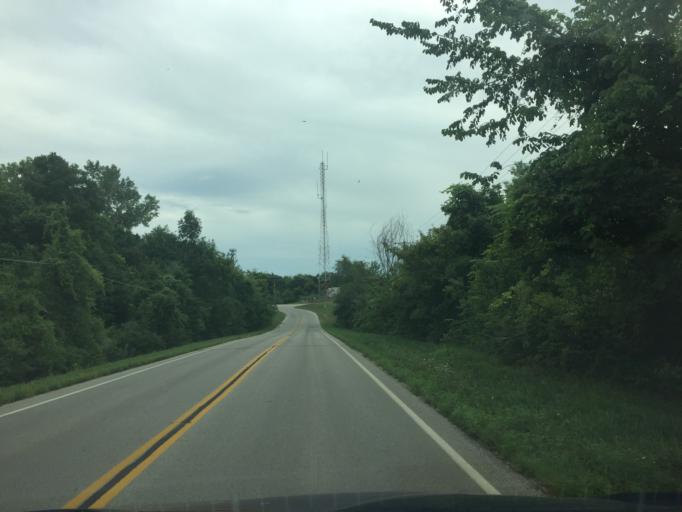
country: US
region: Kansas
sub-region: Leavenworth County
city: Leavenworth
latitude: 39.3624
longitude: -94.9385
